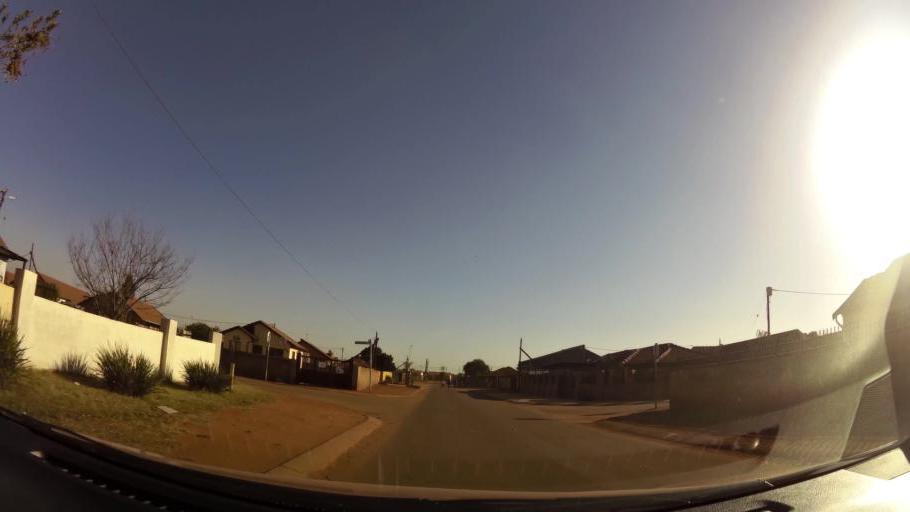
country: ZA
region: Gauteng
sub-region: City of Tshwane Metropolitan Municipality
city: Mabopane
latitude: -25.5891
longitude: 28.0967
